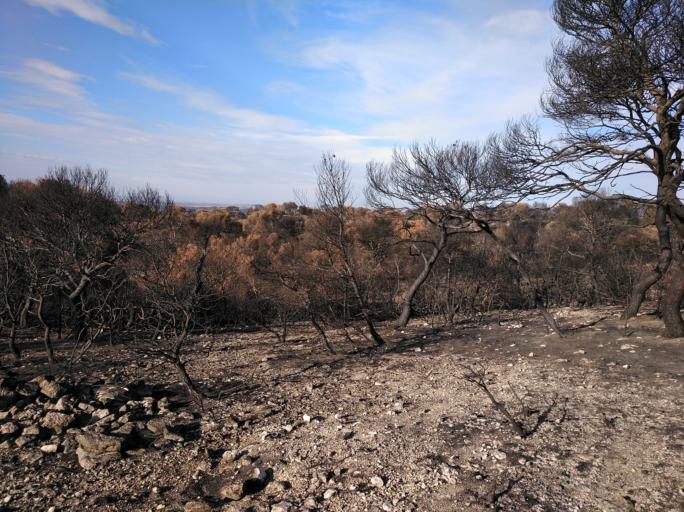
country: ES
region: Aragon
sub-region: Provincia de Zaragoza
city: San Mateo de Gallego
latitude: 41.7583
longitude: -0.7309
